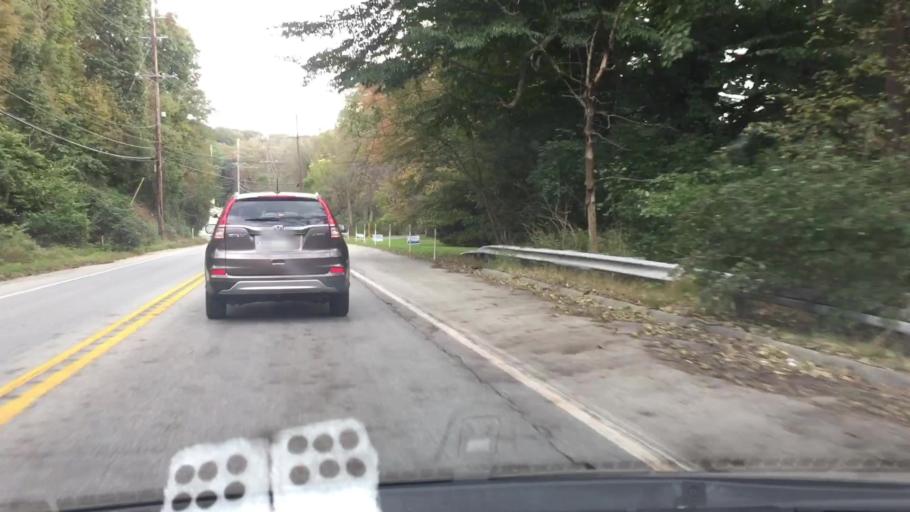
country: US
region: Pennsylvania
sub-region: Delaware County
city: Chester Heights
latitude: 39.9535
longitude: -75.5134
